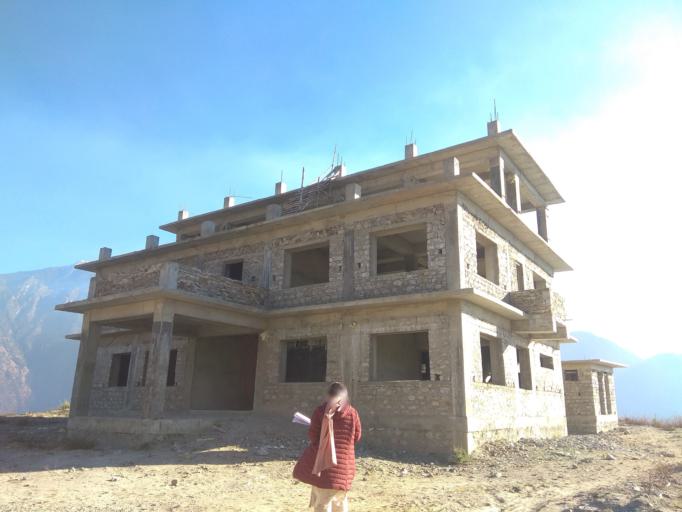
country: NP
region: Far Western
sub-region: Seti Zone
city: Achham
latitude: 29.2444
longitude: 81.6441
